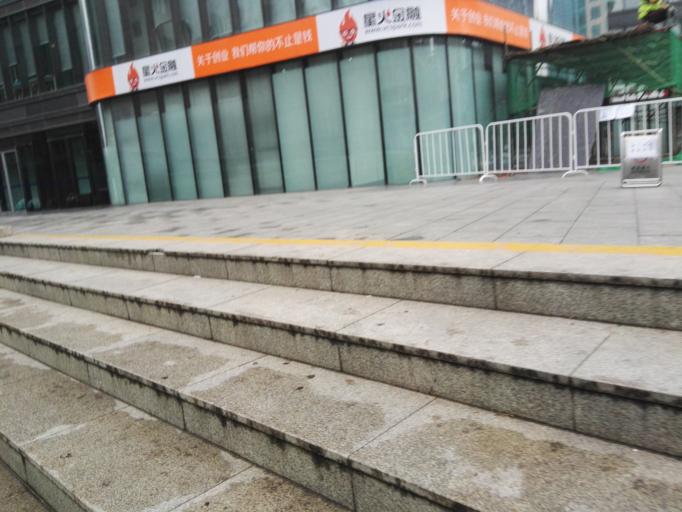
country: CN
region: Beijing
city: Haidian
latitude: 39.9824
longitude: 116.3013
